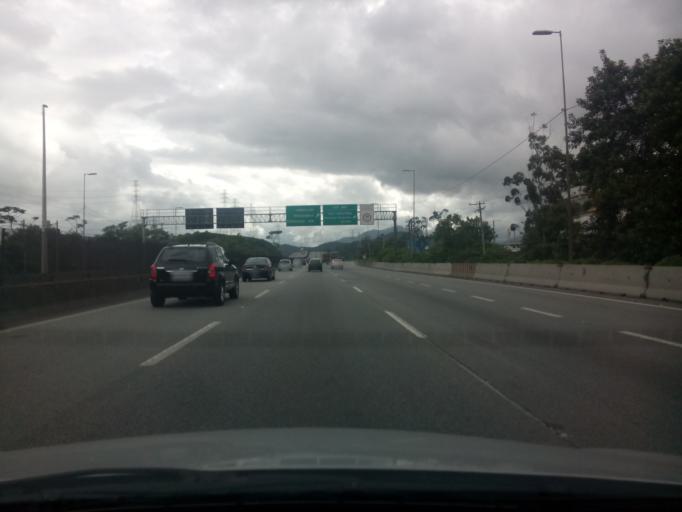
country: BR
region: Sao Paulo
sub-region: Cubatao
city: Cubatao
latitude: -23.8627
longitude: -46.4149
